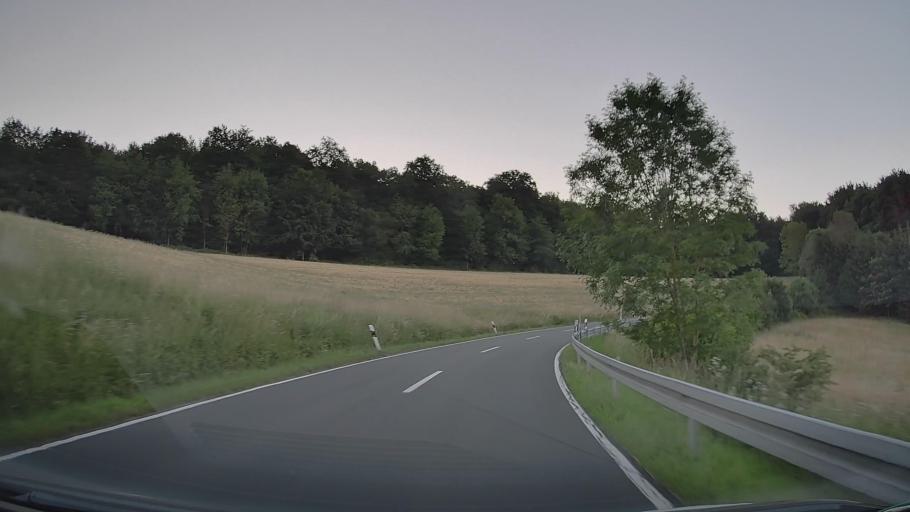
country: DE
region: Lower Saxony
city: Bad Pyrmont
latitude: 51.9976
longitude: 9.2106
